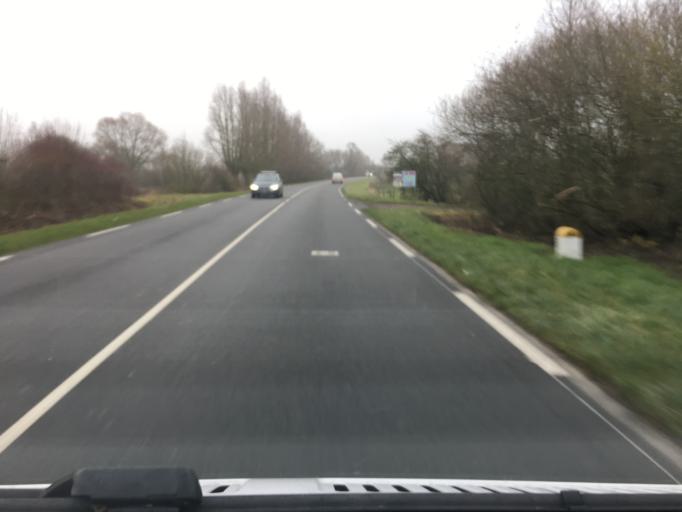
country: FR
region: Picardie
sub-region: Departement de la Somme
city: Saint-Valery-sur-Somme
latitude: 50.1956
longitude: 1.6966
